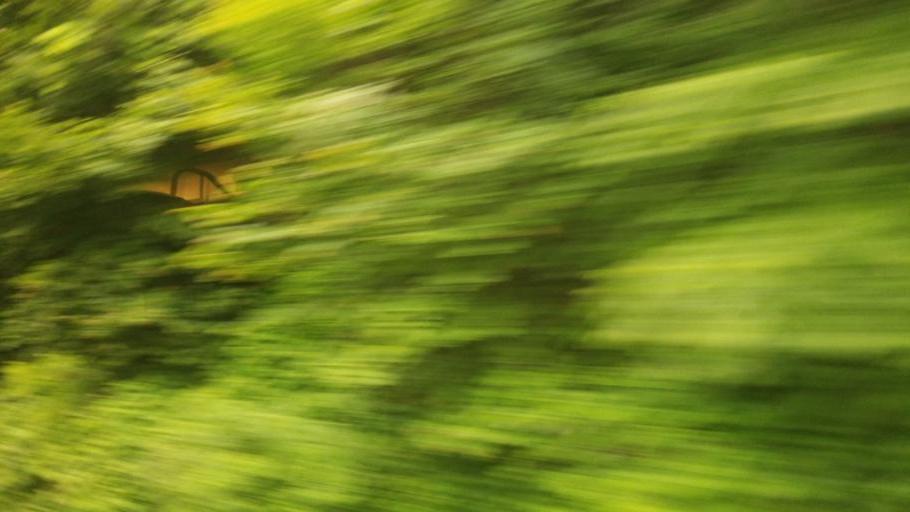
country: US
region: Pennsylvania
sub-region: Somerset County
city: Milford
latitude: 39.8137
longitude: -79.3453
